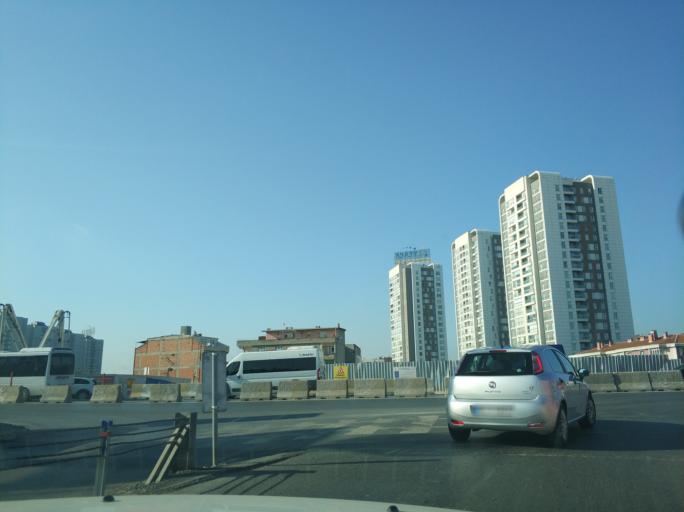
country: TR
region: Istanbul
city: Sultangazi
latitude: 41.0850
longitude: 28.9077
